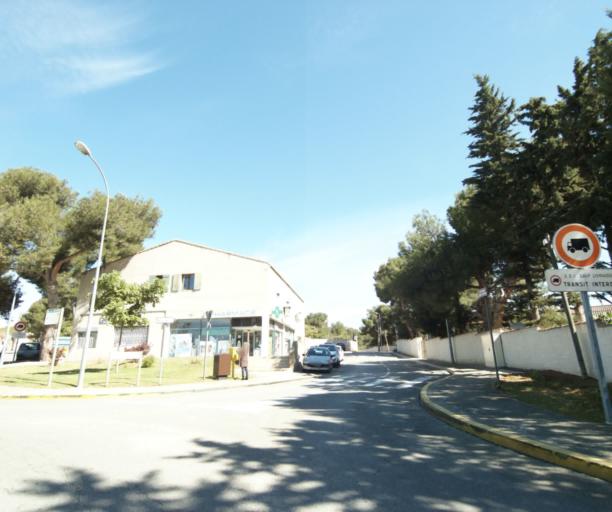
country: FR
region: Provence-Alpes-Cote d'Azur
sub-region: Departement des Bouches-du-Rhone
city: Rognac
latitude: 43.5087
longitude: 5.2186
